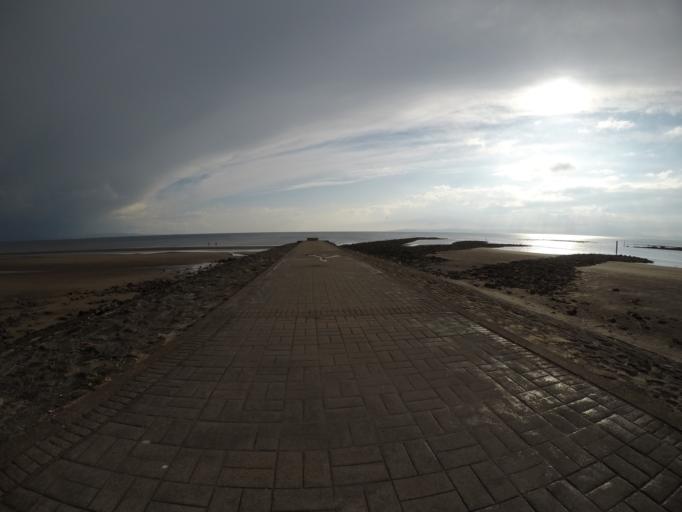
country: GB
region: Scotland
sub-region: North Ayrshire
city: Irvine
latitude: 55.6046
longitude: -4.6949
